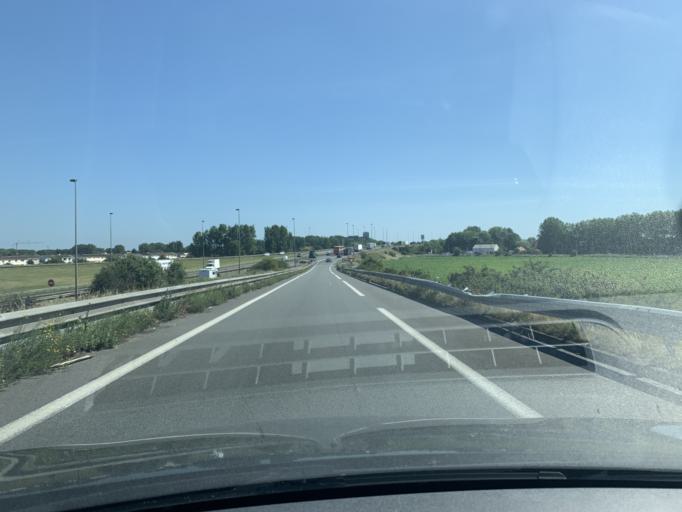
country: FR
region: Nord-Pas-de-Calais
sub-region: Departement du Nord
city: Grande-Synthe
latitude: 51.0078
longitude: 2.3258
